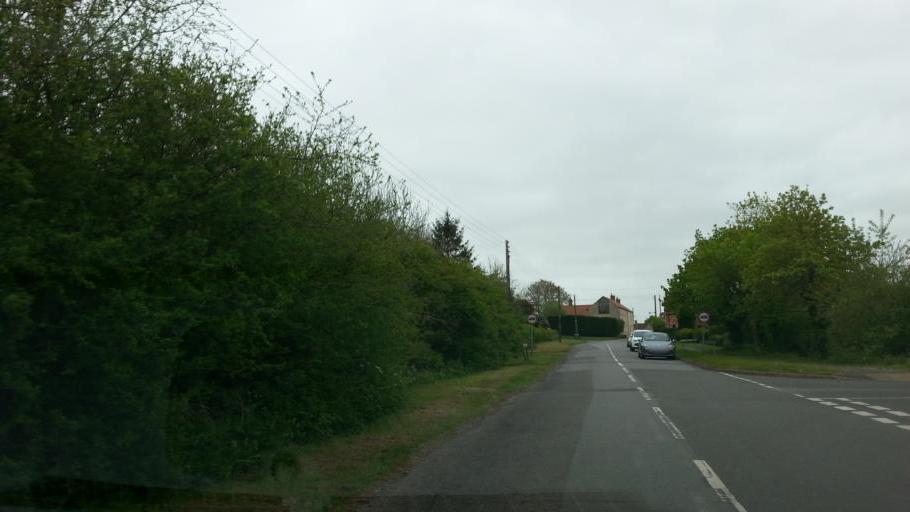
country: GB
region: England
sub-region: District of Rutland
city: Greetham
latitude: 52.8092
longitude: -0.6208
